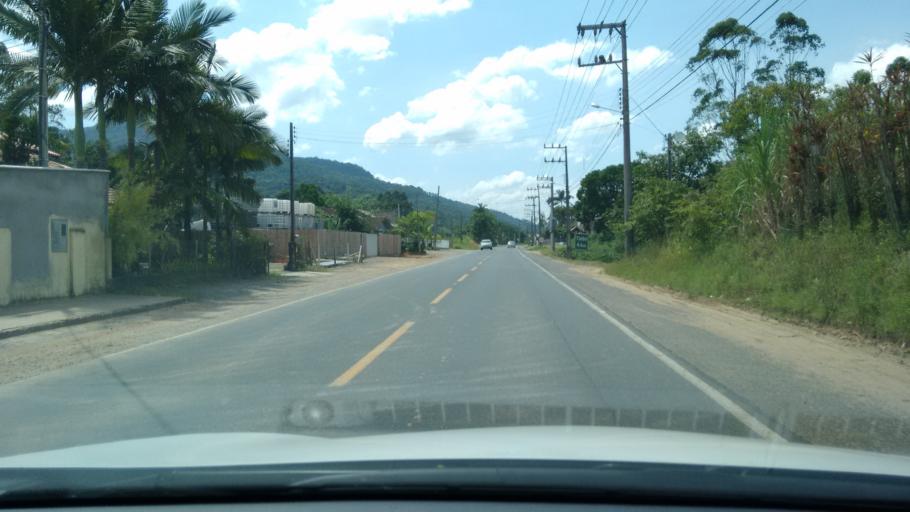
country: BR
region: Santa Catarina
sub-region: Timbo
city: Timbo
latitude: -26.8355
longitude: -49.3235
